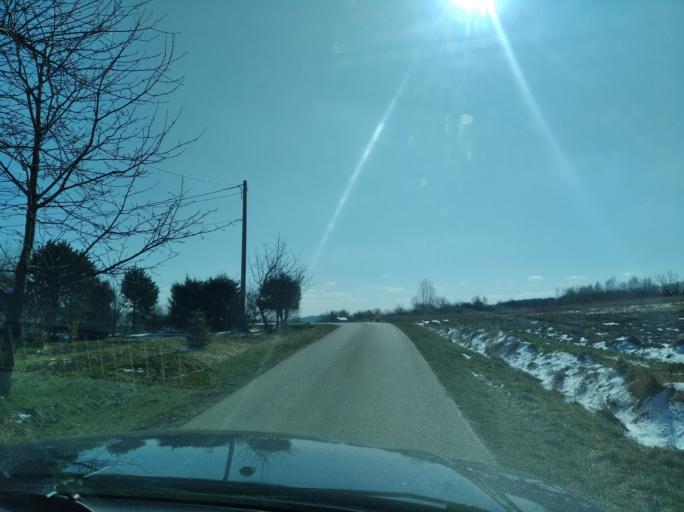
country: PL
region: Subcarpathian Voivodeship
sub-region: Powiat strzyzowski
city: Gwoznica Gorna
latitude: 49.8209
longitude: 22.0114
